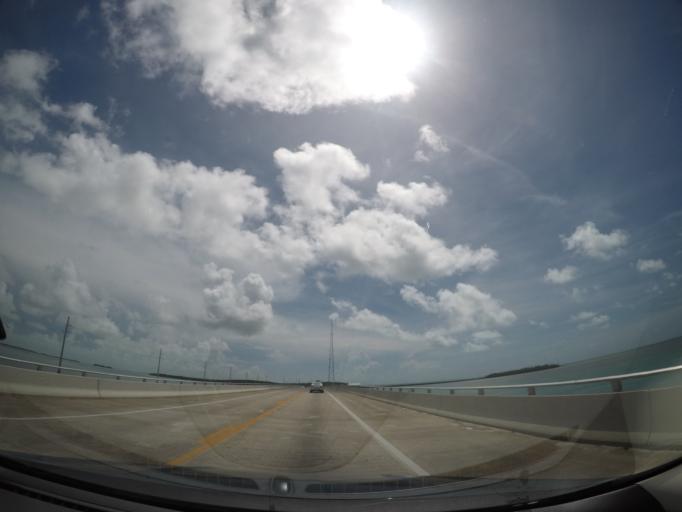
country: US
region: Florida
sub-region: Monroe County
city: Islamorada
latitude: 24.8940
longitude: -80.6673
